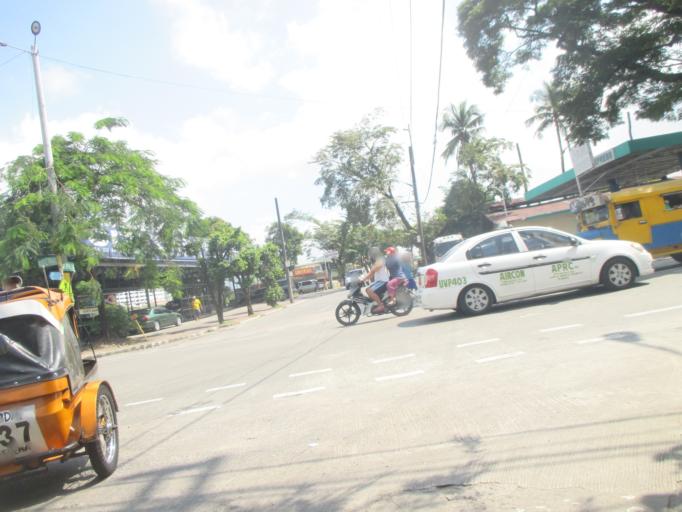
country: PH
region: Metro Manila
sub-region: Marikina
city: Calumpang
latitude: 14.6328
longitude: 121.1013
